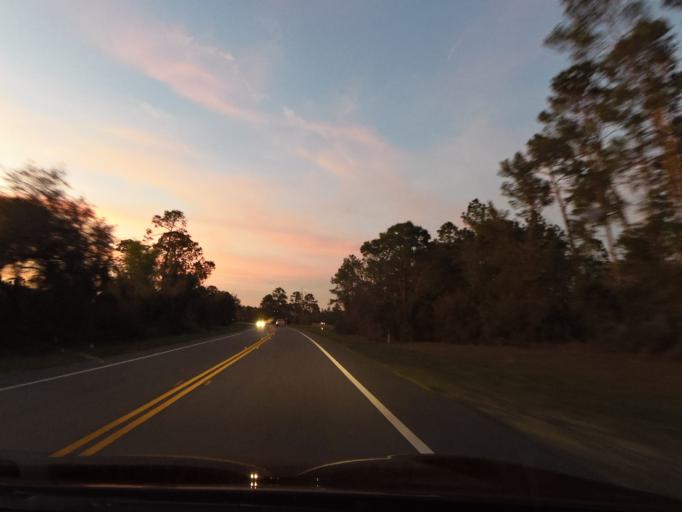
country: US
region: Florida
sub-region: Volusia County
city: De Leon Springs
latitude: 29.1828
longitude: -81.3046
